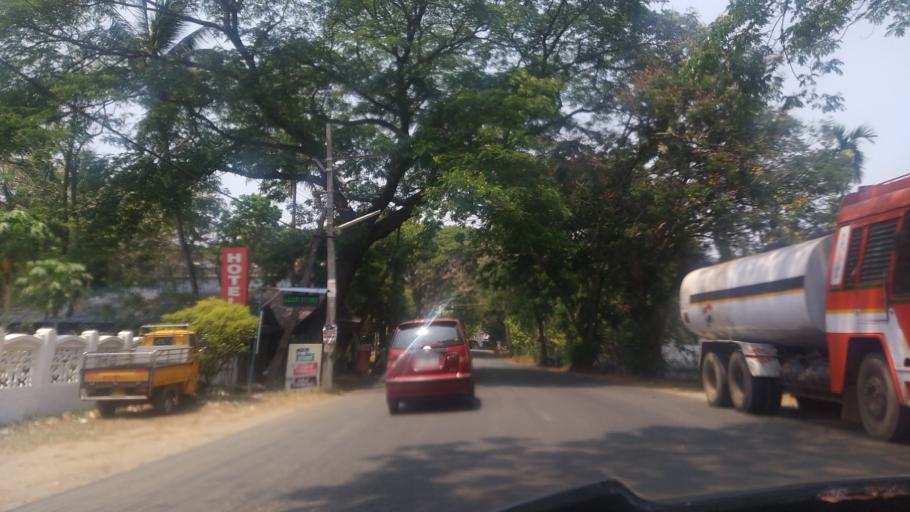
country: IN
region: Kerala
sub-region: Thrissur District
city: Kodungallur
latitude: 10.2582
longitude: 76.1839
